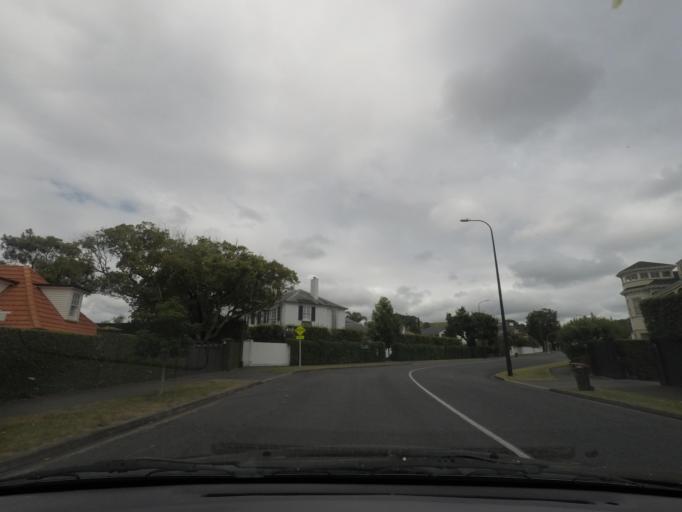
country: NZ
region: Auckland
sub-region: Auckland
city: Auckland
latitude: -36.8721
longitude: 174.7857
